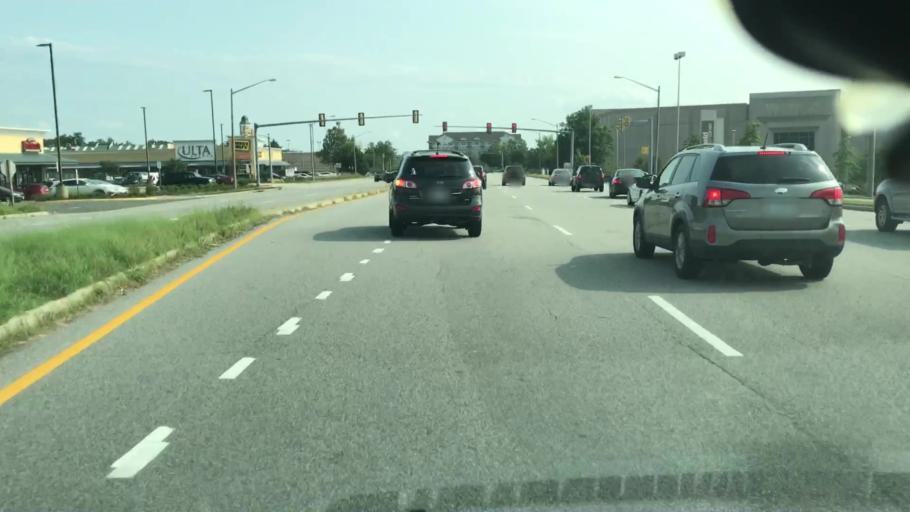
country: US
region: Virginia
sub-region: Fairfax County
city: Springfield
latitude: 38.7758
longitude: -77.1717
